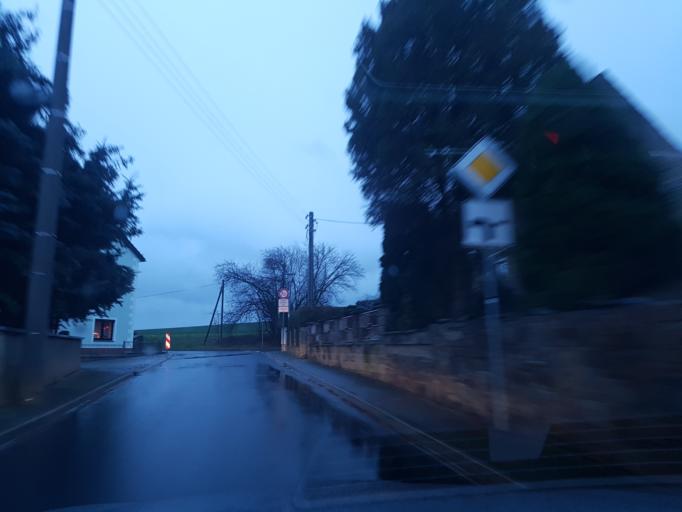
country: DE
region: Saxony
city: Priestewitz
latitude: 51.2423
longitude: 13.5195
